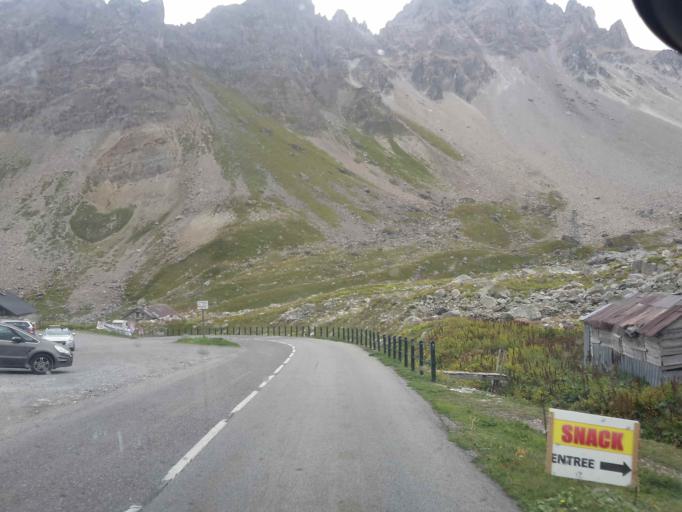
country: FR
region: Rhone-Alpes
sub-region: Departement de la Savoie
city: Valloire
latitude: 45.0794
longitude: 6.4219
